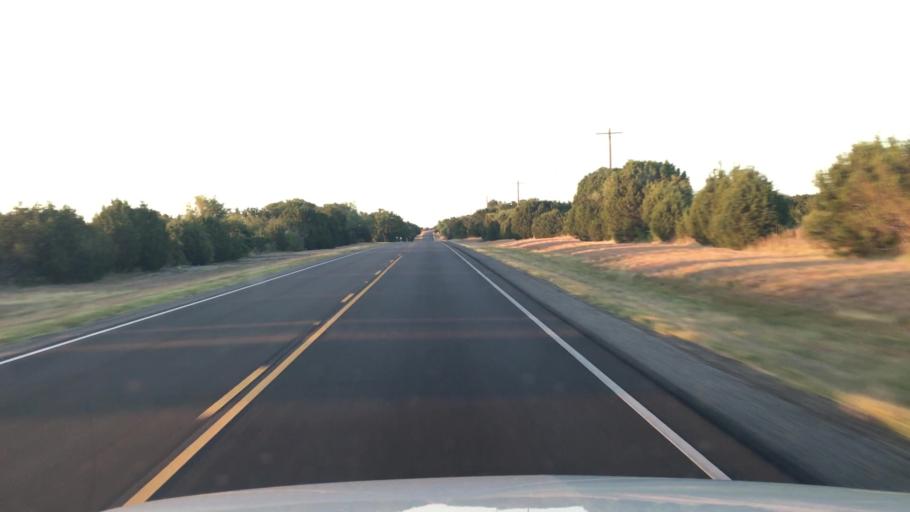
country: US
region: Texas
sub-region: Hamilton County
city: Hico
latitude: 32.0501
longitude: -98.0012
